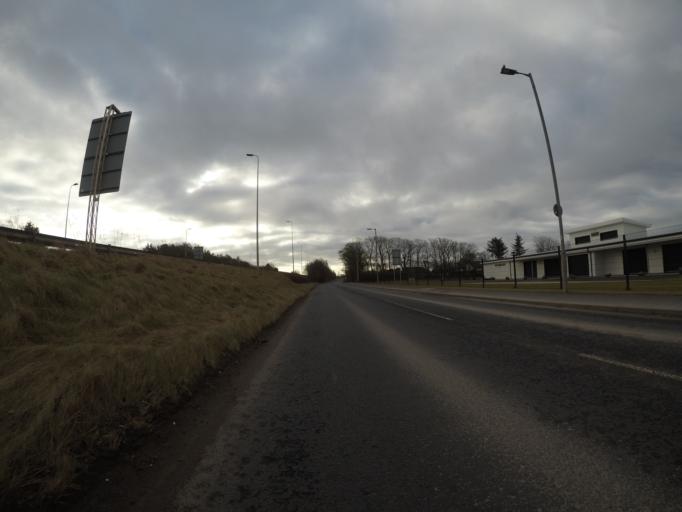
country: GB
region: Scotland
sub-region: North Ayrshire
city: Dreghorn
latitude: 55.5723
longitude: -4.6402
